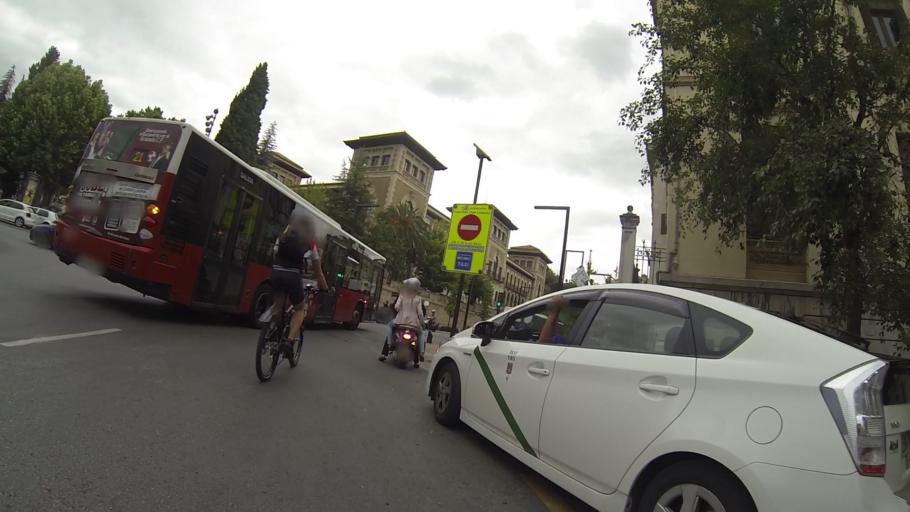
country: ES
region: Andalusia
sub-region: Provincia de Granada
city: Granada
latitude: 37.1829
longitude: -3.6022
